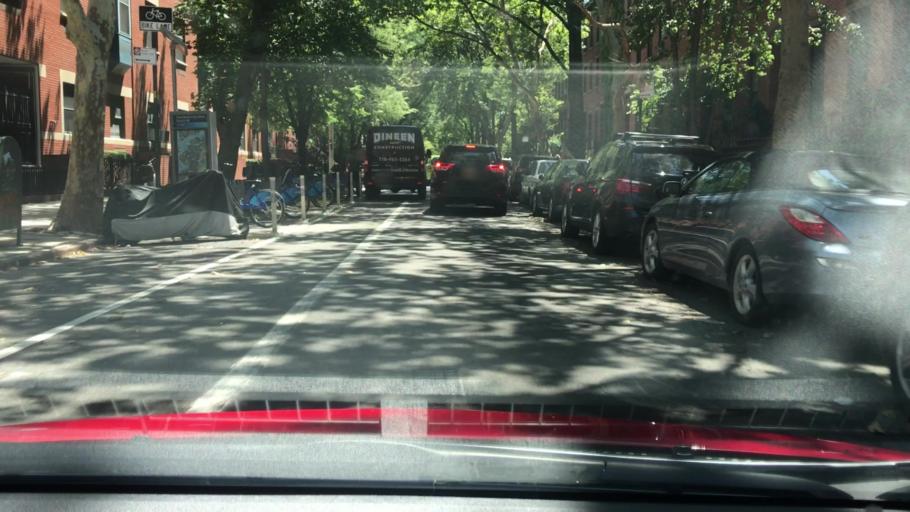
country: US
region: New York
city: New York City
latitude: 40.6866
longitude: -73.9879
